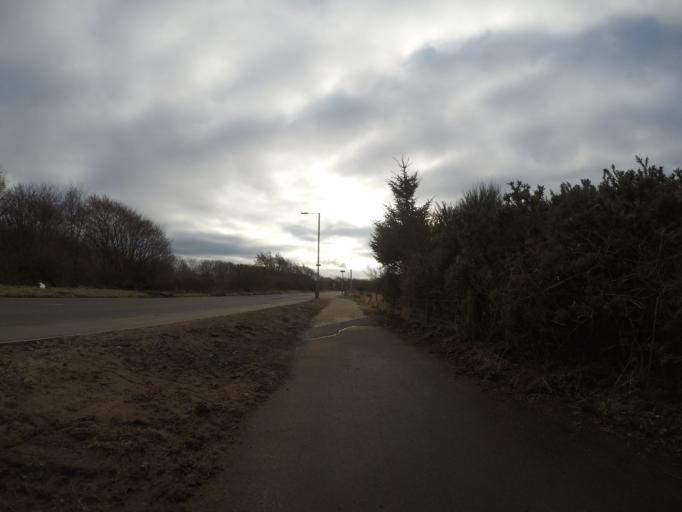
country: GB
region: Scotland
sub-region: North Ayrshire
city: Irvine
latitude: 55.5932
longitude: -4.6538
